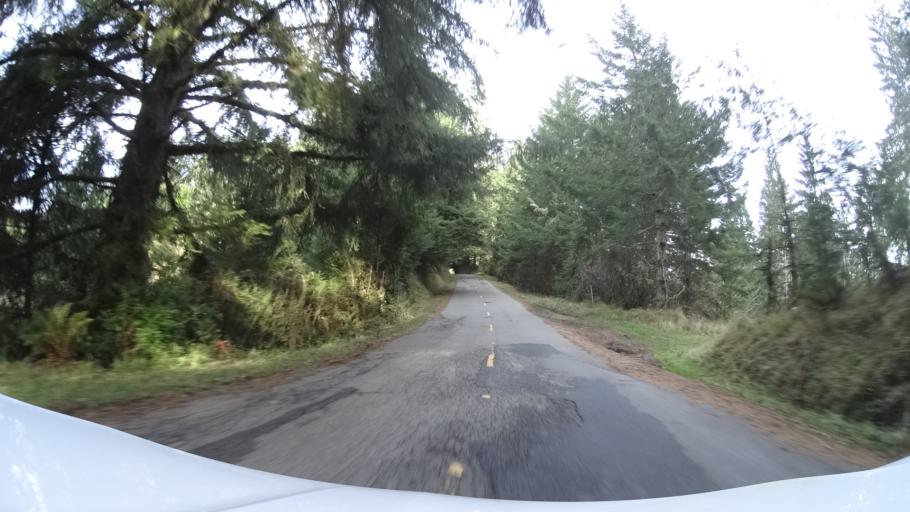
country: US
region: California
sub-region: Humboldt County
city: Ferndale
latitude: 40.5283
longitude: -124.2696
